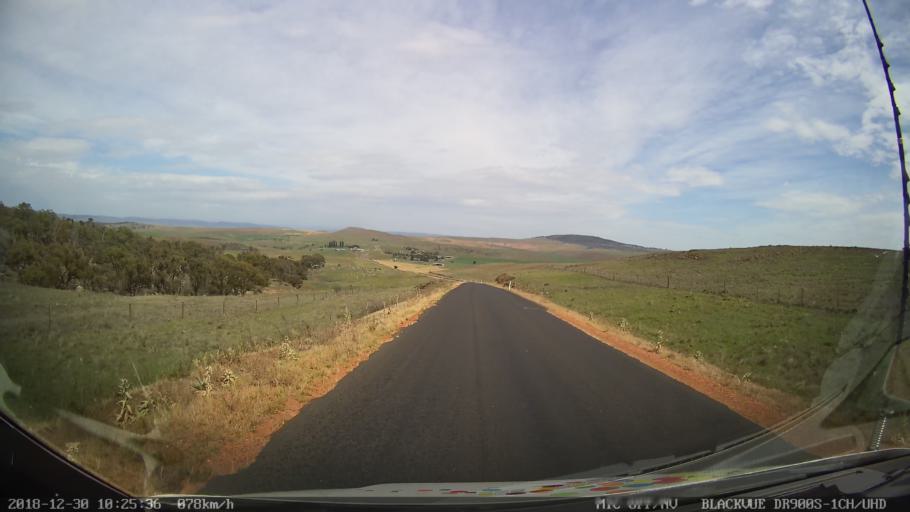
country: AU
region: New South Wales
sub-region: Snowy River
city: Berridale
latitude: -36.5231
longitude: 148.9573
